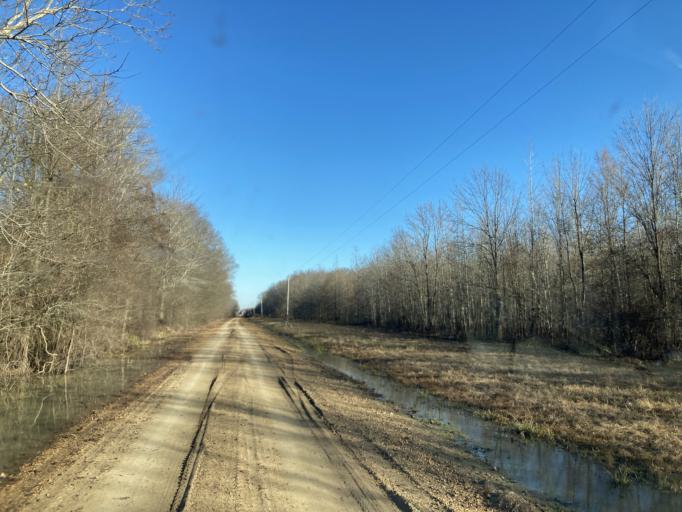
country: US
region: Mississippi
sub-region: Sharkey County
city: Rolling Fork
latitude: 32.9344
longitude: -90.6565
